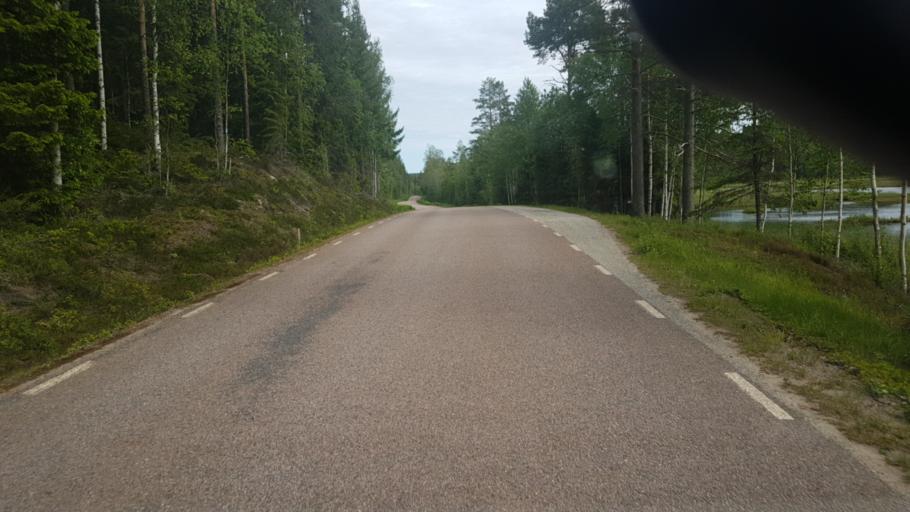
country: SE
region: Vaermland
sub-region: Arvika Kommun
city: Arvika
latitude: 59.8100
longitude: 12.8327
